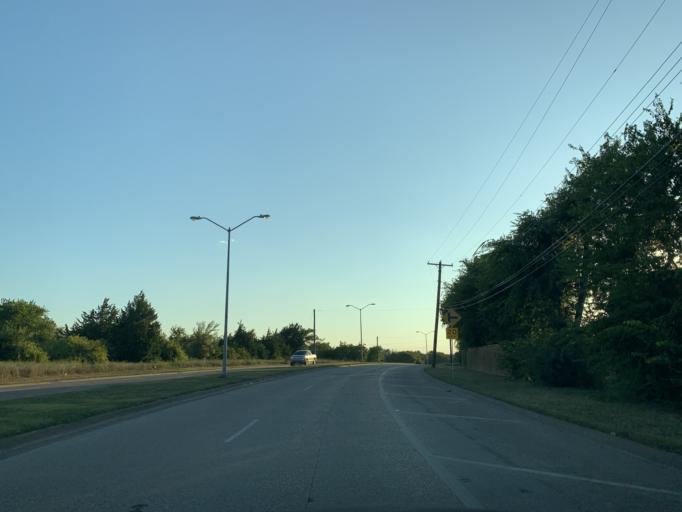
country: US
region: Texas
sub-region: Dallas County
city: Lancaster
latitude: 32.6626
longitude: -96.8025
